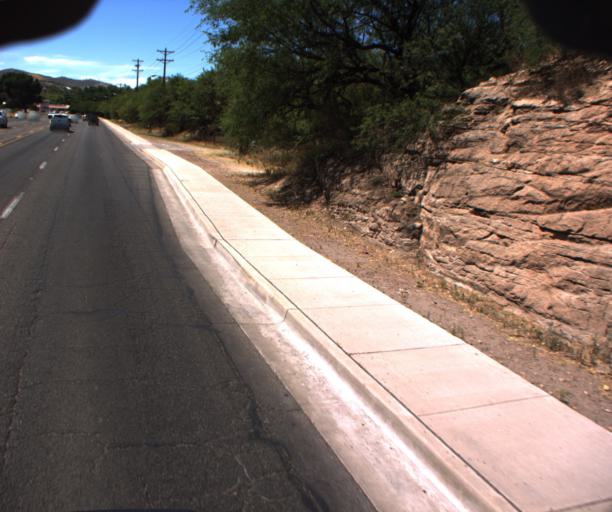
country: US
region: Arizona
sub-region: Santa Cruz County
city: Nogales
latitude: 31.3598
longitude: -110.9305
